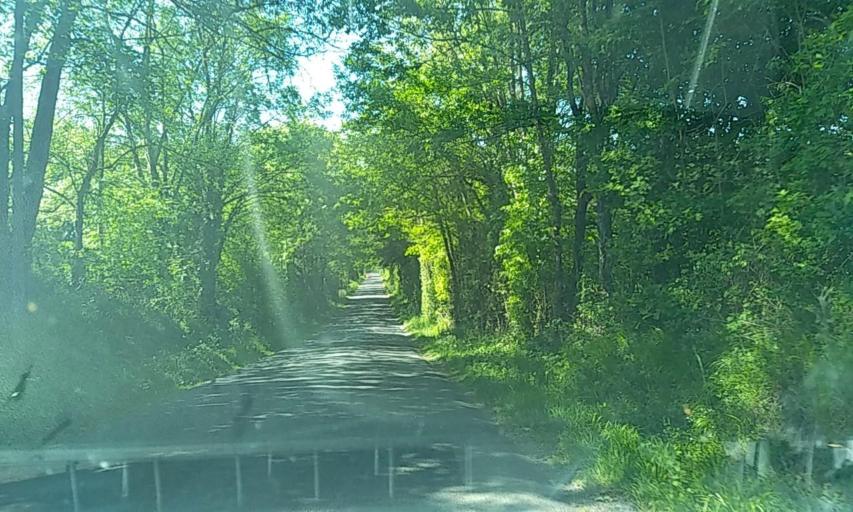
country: FR
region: Poitou-Charentes
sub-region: Departement des Deux-Sevres
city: Boisme
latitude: 46.7811
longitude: -0.4467
